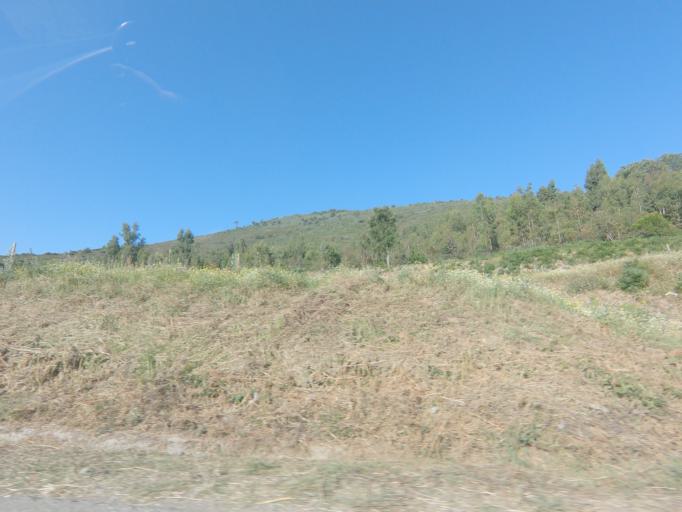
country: PT
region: Vila Real
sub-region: Sabrosa
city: Vilela
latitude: 41.2310
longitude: -7.5700
